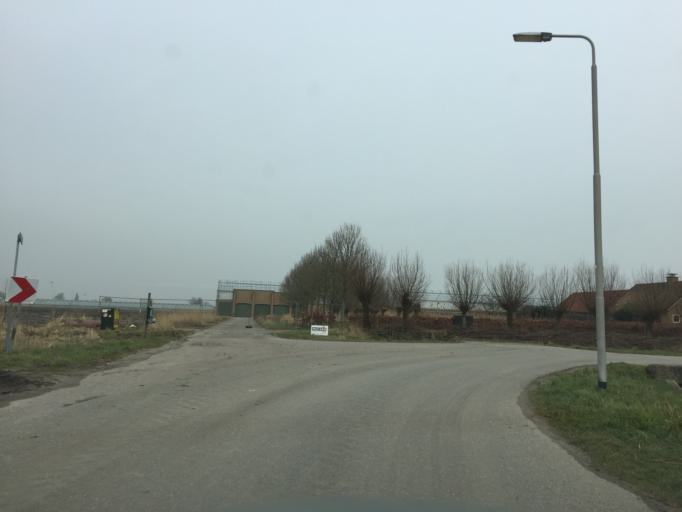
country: NL
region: South Holland
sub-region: Gemeente Pijnacker-Nootdorp
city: Pijnacker
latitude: 52.0254
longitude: 4.4488
